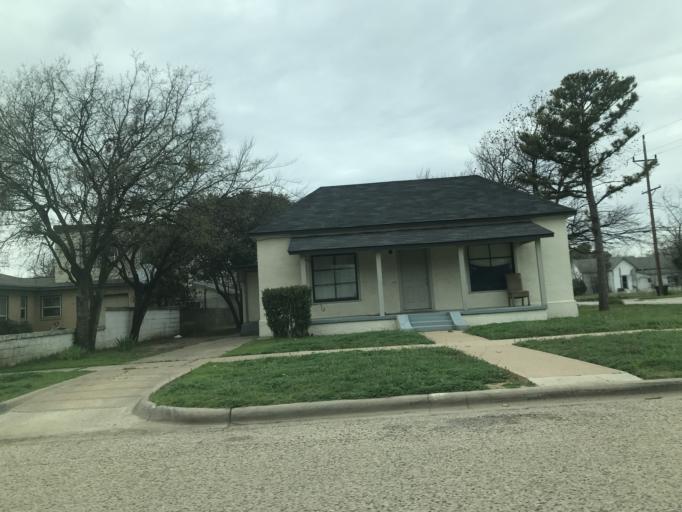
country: US
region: Texas
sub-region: Taylor County
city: Abilene
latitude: 32.4607
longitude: -99.7381
